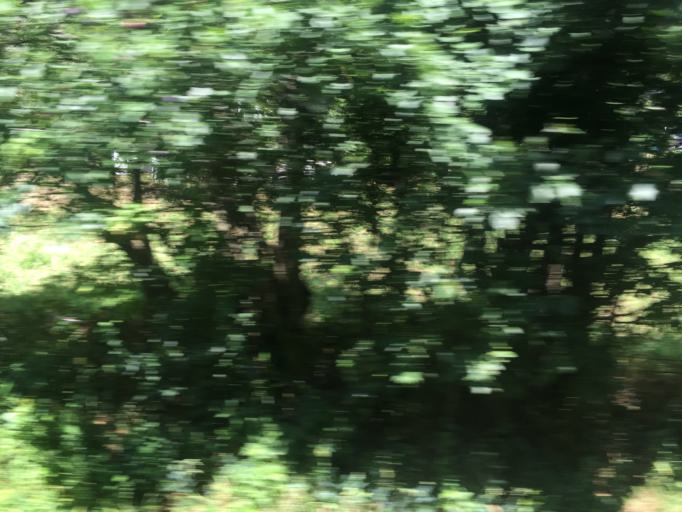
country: CH
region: Valais
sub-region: Goms District
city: Fiesch
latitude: 46.3776
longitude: 8.1006
